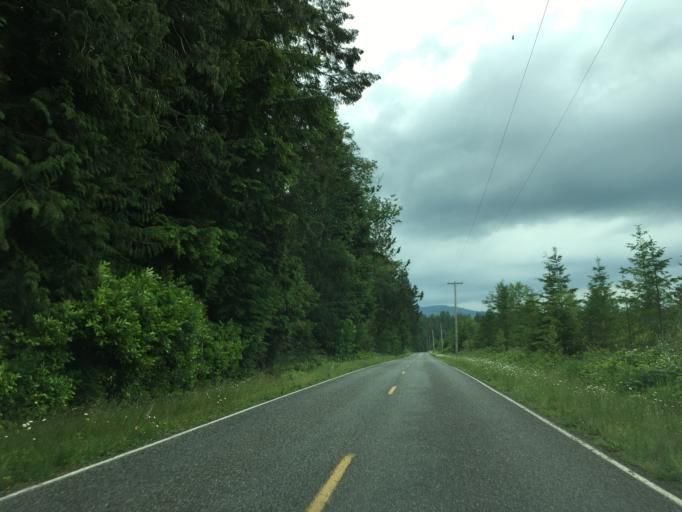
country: US
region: Washington
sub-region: Whatcom County
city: Peaceful Valley
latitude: 48.9835
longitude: -122.1138
